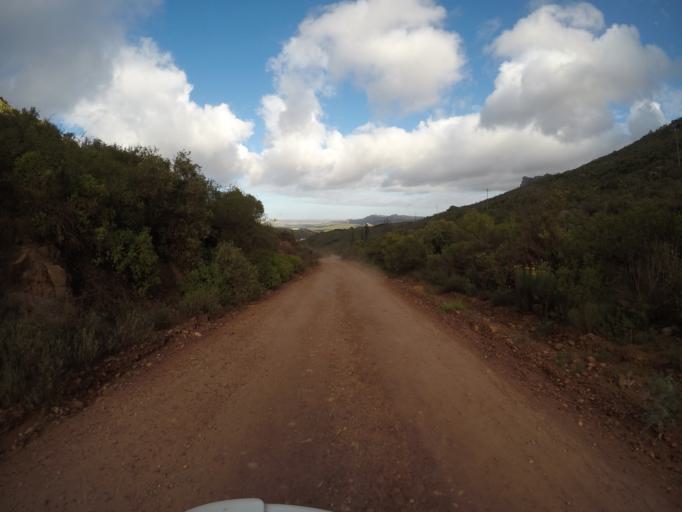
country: ZA
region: Western Cape
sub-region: West Coast District Municipality
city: Clanwilliam
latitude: -32.3402
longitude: 18.7829
